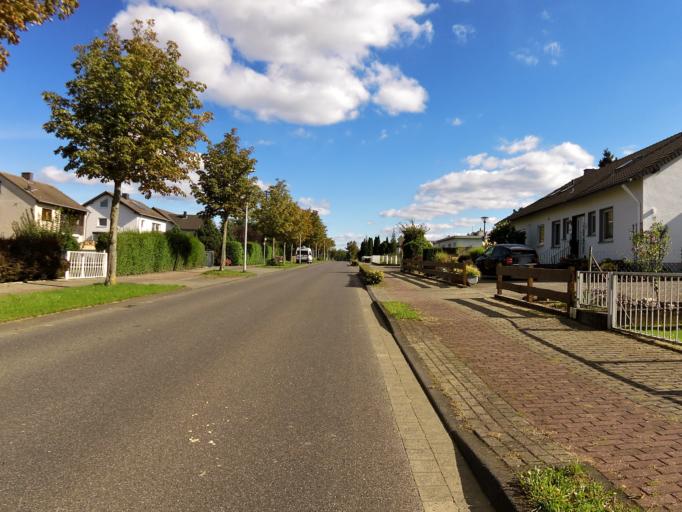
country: DE
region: North Rhine-Westphalia
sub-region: Regierungsbezirk Koln
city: Euskirchen
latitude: 50.6221
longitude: 6.8581
